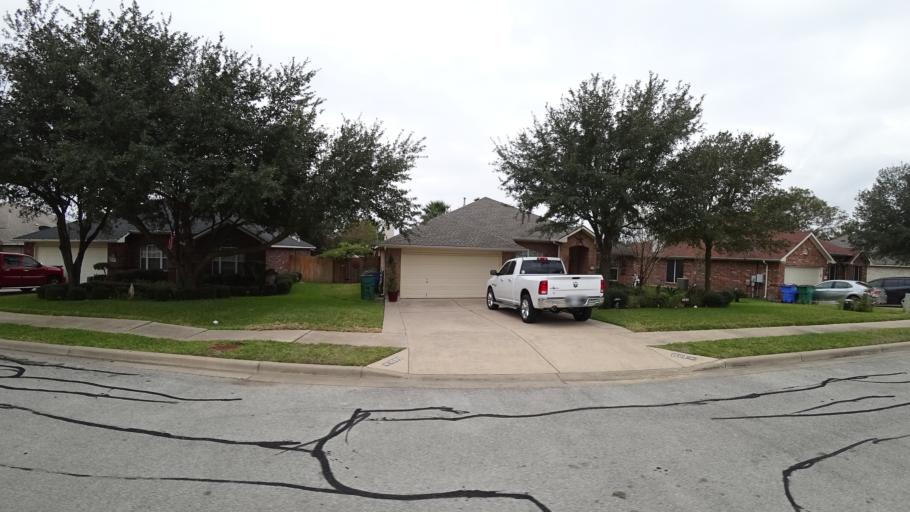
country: US
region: Texas
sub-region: Travis County
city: Pflugerville
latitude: 30.4353
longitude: -97.6054
